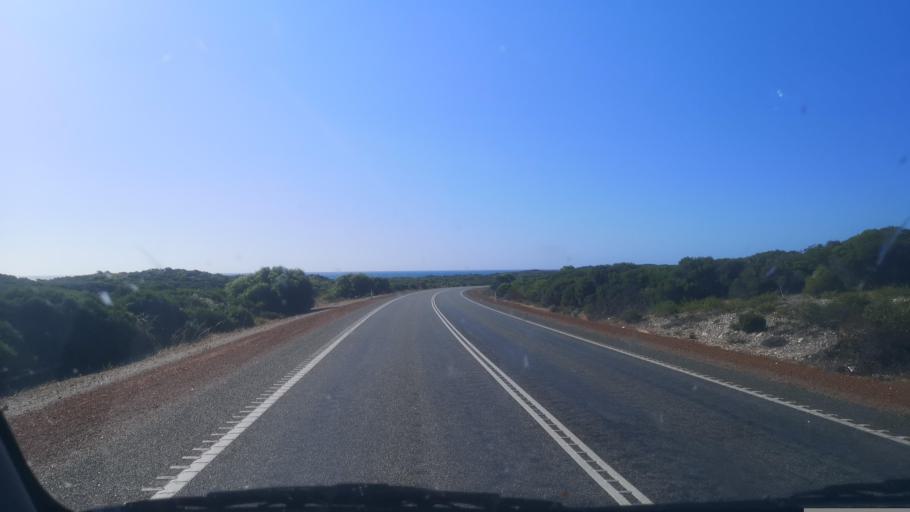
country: AU
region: Western Australia
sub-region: Dandaragan
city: Jurien Bay
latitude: -30.6616
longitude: 115.1406
